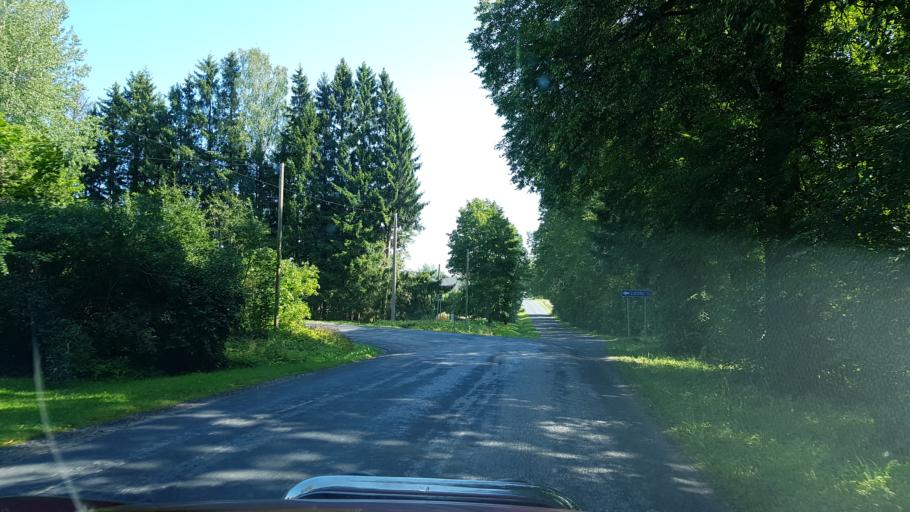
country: EE
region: Vorumaa
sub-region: Voru linn
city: Voru
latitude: 57.7472
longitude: 27.2675
